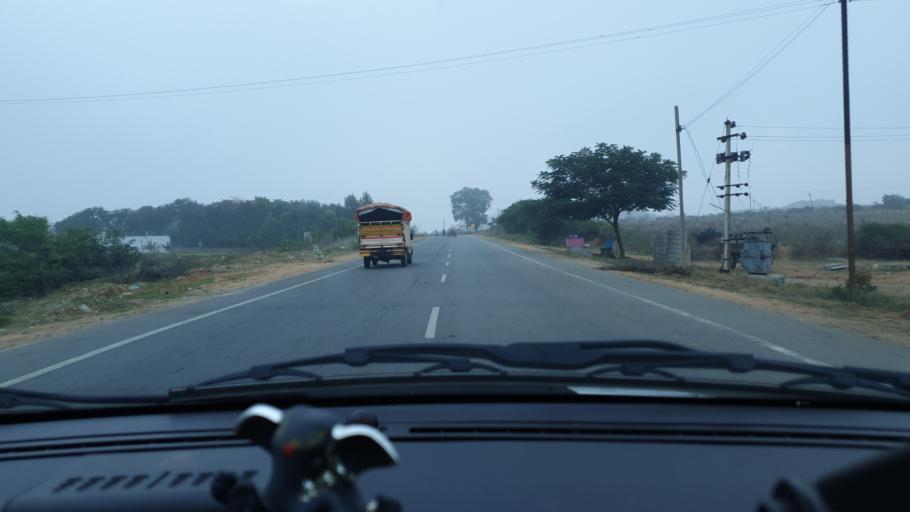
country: IN
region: Telangana
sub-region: Mahbubnagar
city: Farrukhnagar
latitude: 16.9468
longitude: 78.5241
